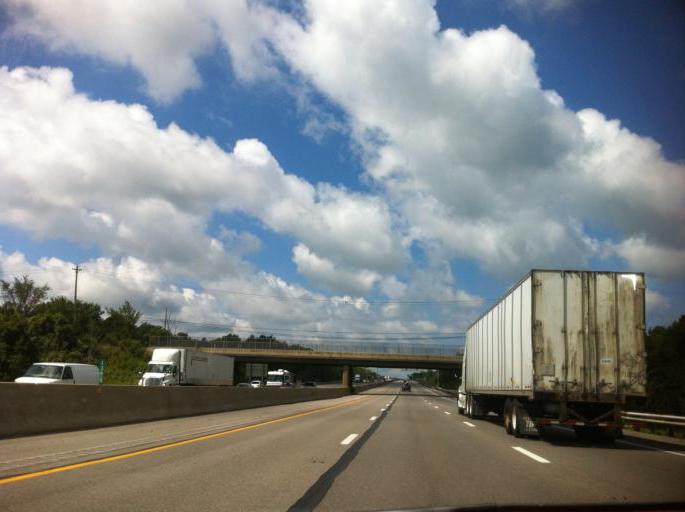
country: US
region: Ohio
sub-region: Lorain County
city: Amherst
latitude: 41.3775
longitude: -82.2356
